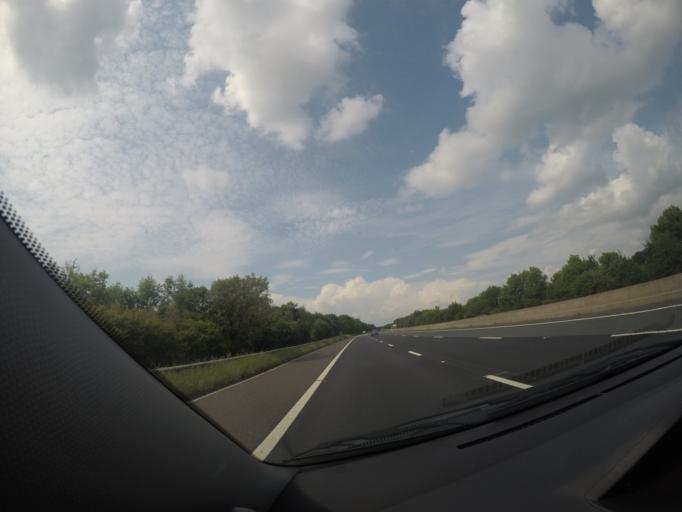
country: GB
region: England
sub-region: Cumbria
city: Scotby
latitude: 54.8213
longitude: -2.8879
